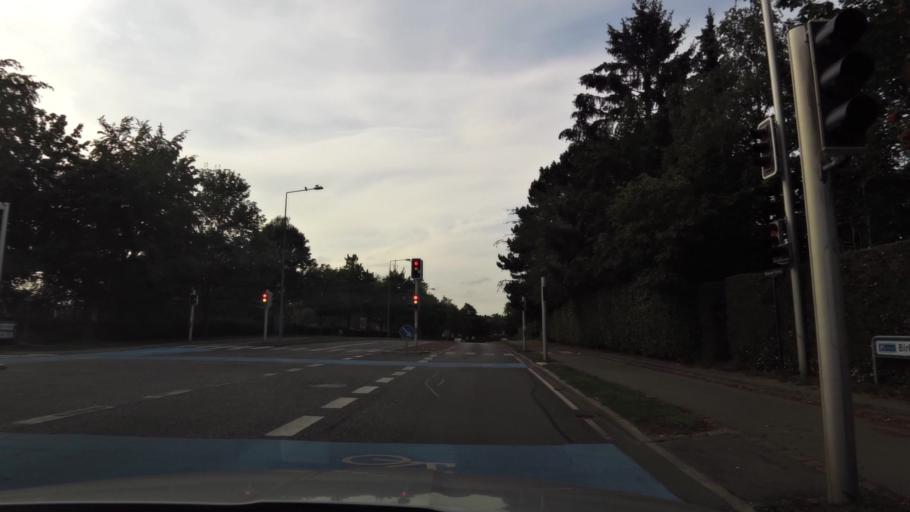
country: DK
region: Capital Region
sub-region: Rudersdal Kommune
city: Birkerod
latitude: 55.8361
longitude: 12.4167
